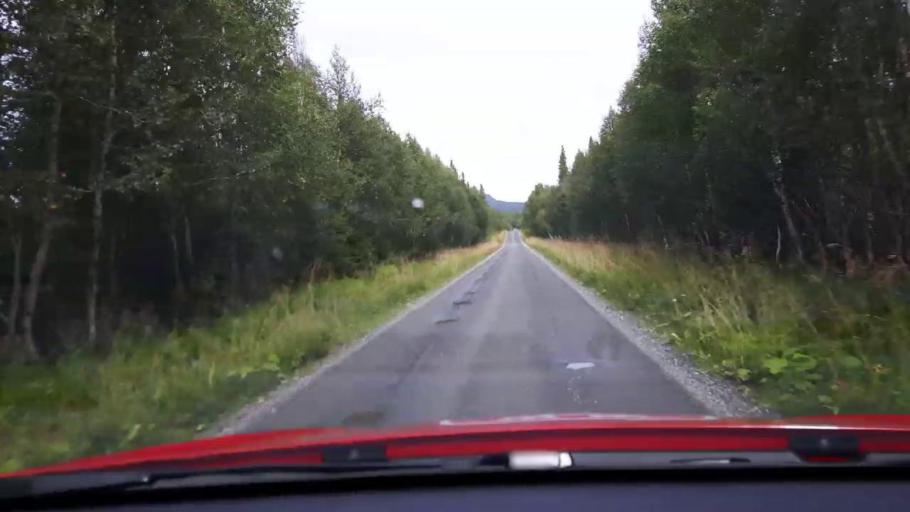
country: SE
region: Jaemtland
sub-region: Are Kommun
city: Are
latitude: 63.7766
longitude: 13.0972
